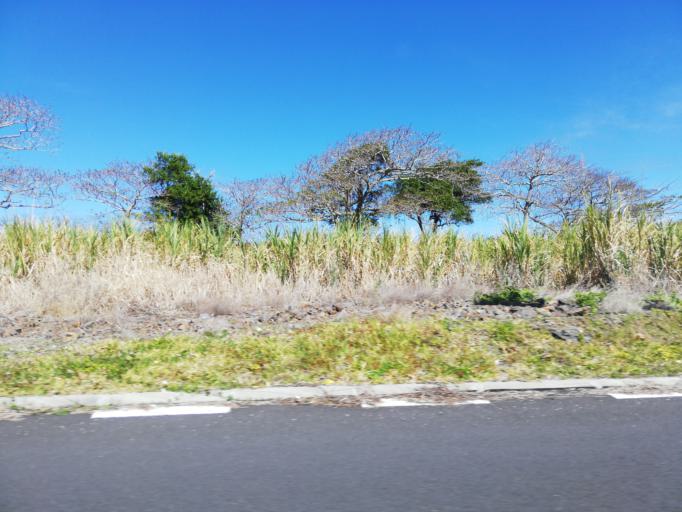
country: MU
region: Grand Port
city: Beau Vallon
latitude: -20.4525
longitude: 57.6948
